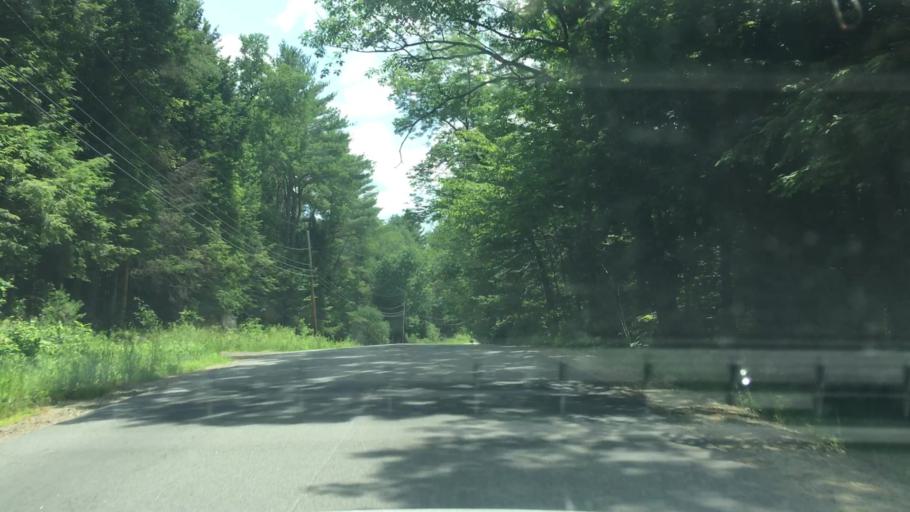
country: US
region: New Hampshire
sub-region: Grafton County
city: Enfield
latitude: 43.6573
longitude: -72.0967
